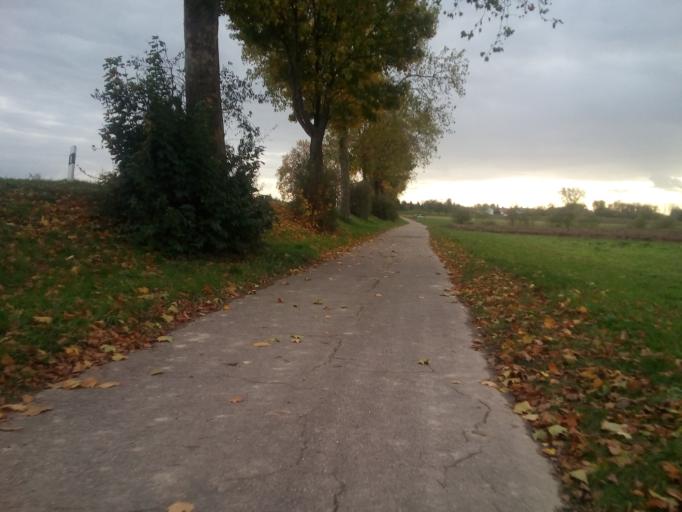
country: DE
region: Baden-Wuerttemberg
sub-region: Karlsruhe Region
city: Lichtenau
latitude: 48.7373
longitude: 8.0097
